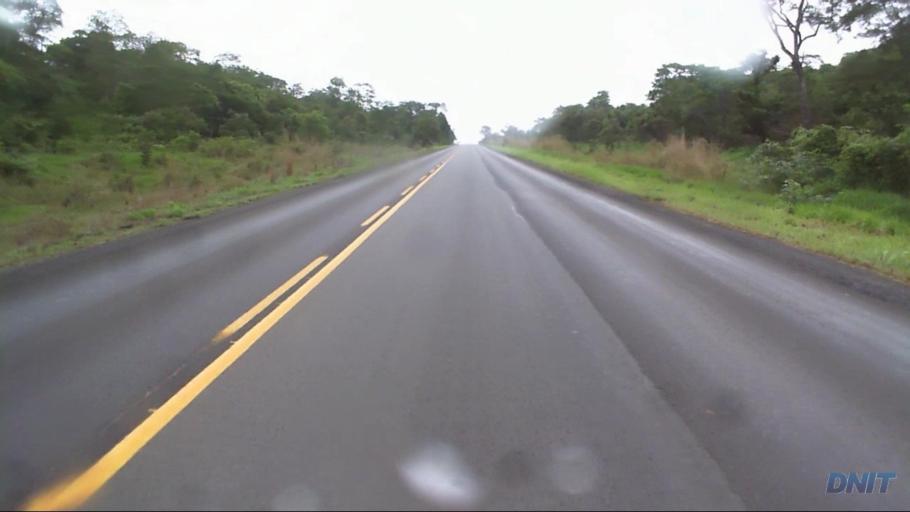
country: BR
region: Goias
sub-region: Padre Bernardo
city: Padre Bernardo
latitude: -15.2048
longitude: -48.4615
